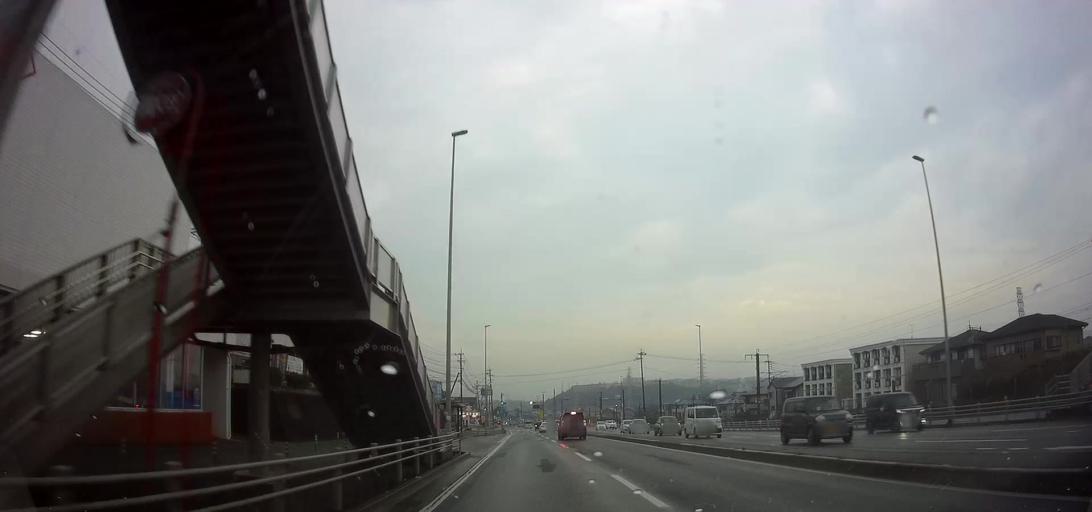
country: JP
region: Nagasaki
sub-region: Isahaya-shi
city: Isahaya
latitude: 32.8412
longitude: 130.0321
